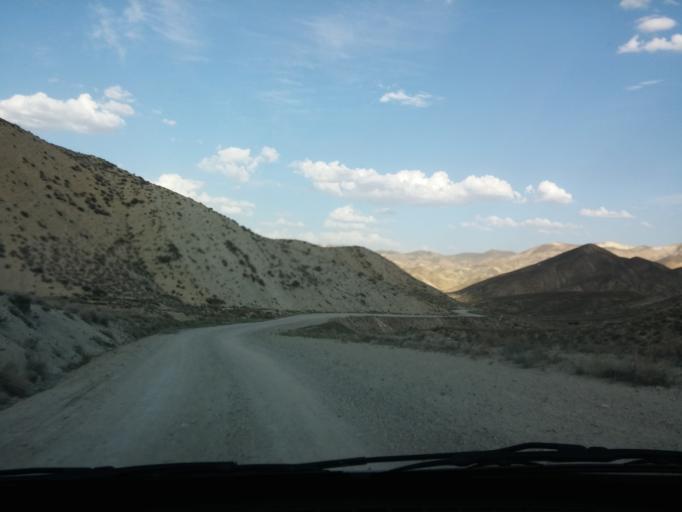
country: IR
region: Tehran
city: Damavand
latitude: 35.5384
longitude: 52.2158
